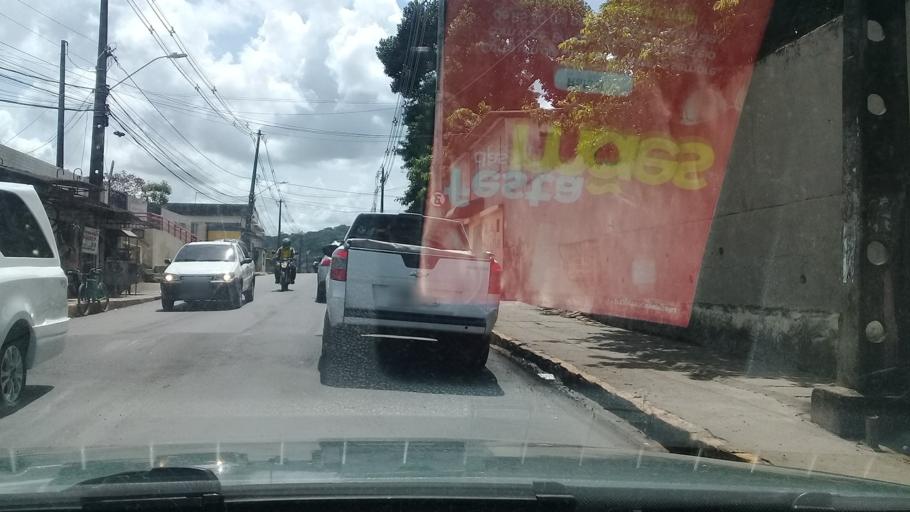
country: BR
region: Pernambuco
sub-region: Jaboatao Dos Guararapes
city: Jaboatao dos Guararapes
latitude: -8.0981
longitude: -35.0206
